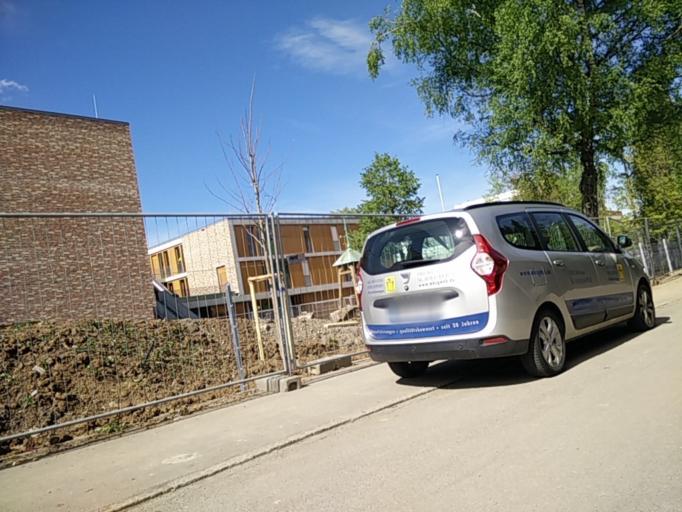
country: DE
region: Baden-Wuerttemberg
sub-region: Regierungsbezirk Stuttgart
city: Boeblingen
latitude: 48.6829
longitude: 9.0050
